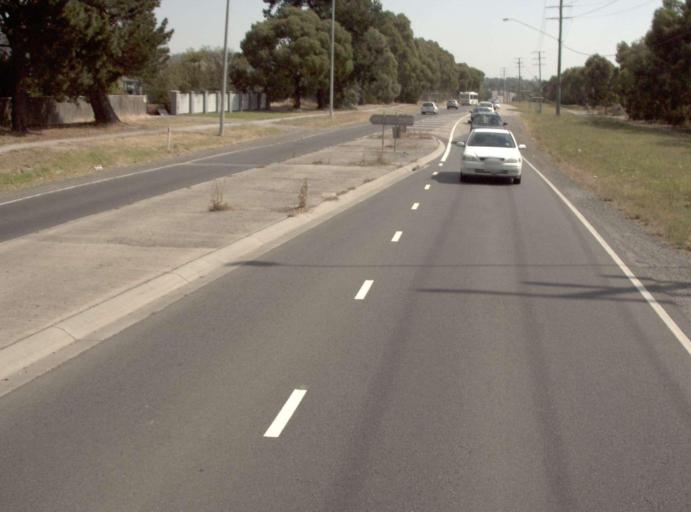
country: AU
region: Victoria
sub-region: Knox
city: Ferntree Gully
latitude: -37.9065
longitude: 145.2800
